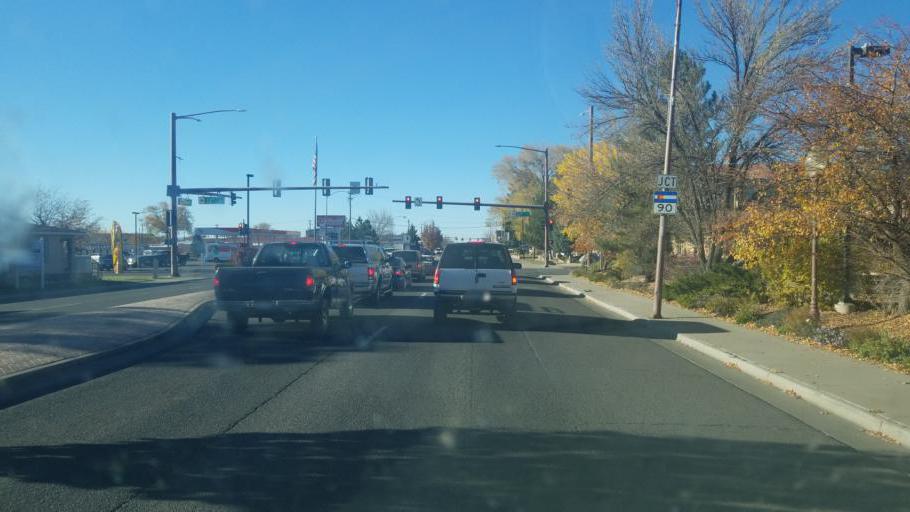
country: US
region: Colorado
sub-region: Montrose County
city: Montrose
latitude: 38.4768
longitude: -107.8755
